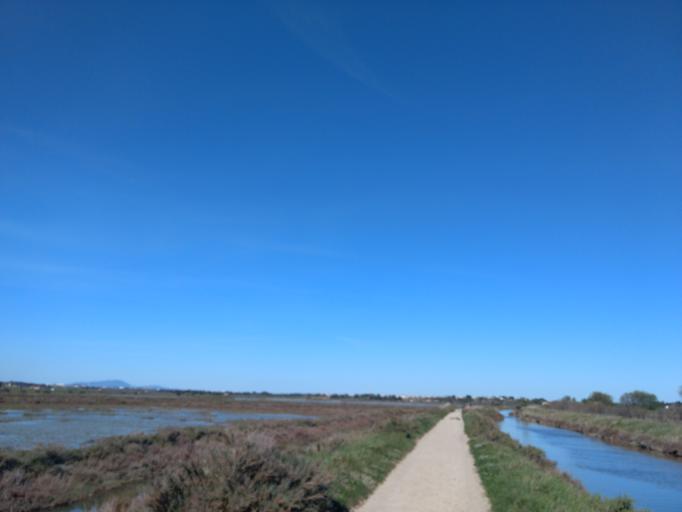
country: FR
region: Languedoc-Roussillon
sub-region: Departement de l'Herault
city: Villeneuve-les-Maguelone
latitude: 43.5106
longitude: 3.8397
